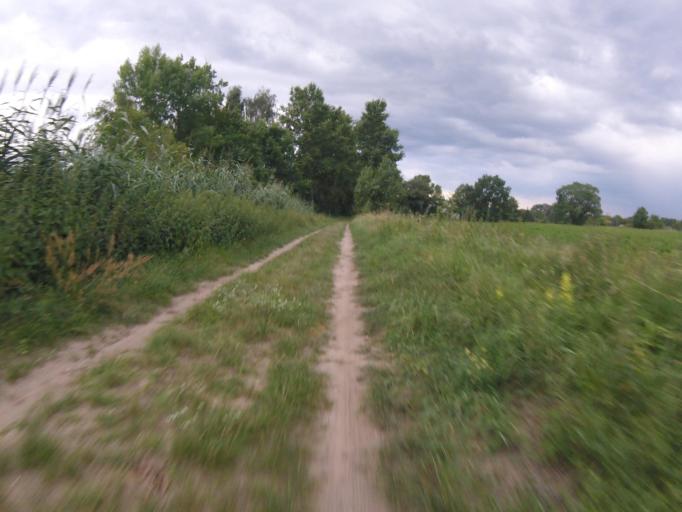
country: DE
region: Brandenburg
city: Mittenwalde
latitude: 52.2728
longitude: 13.5327
